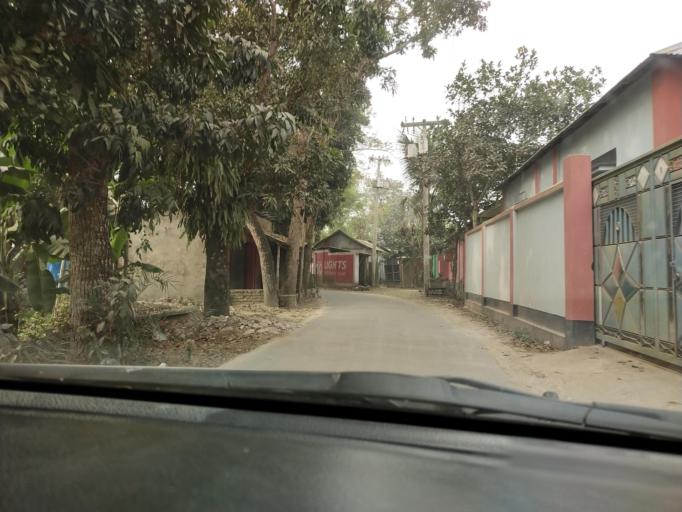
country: BD
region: Dhaka
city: Narsingdi
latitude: 24.0363
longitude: 90.7284
